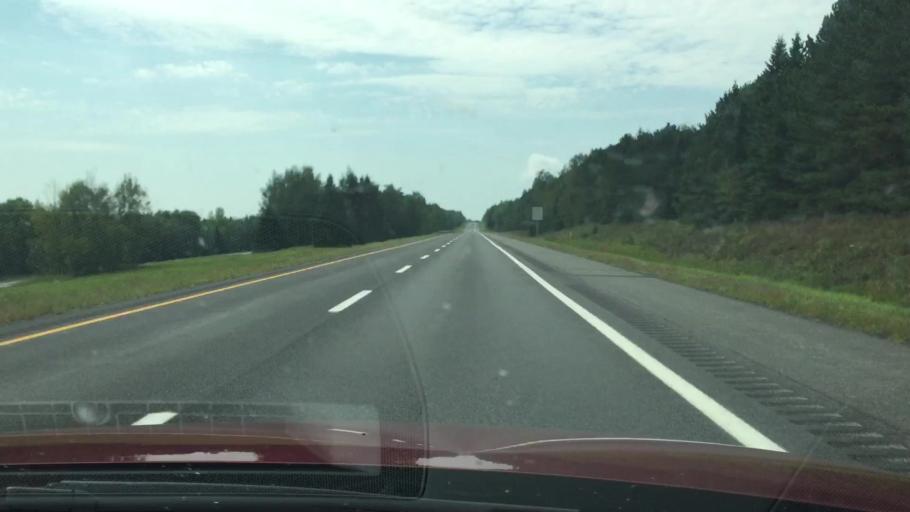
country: US
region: Maine
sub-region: Aroostook County
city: Hodgdon
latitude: 46.1329
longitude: -68.0895
